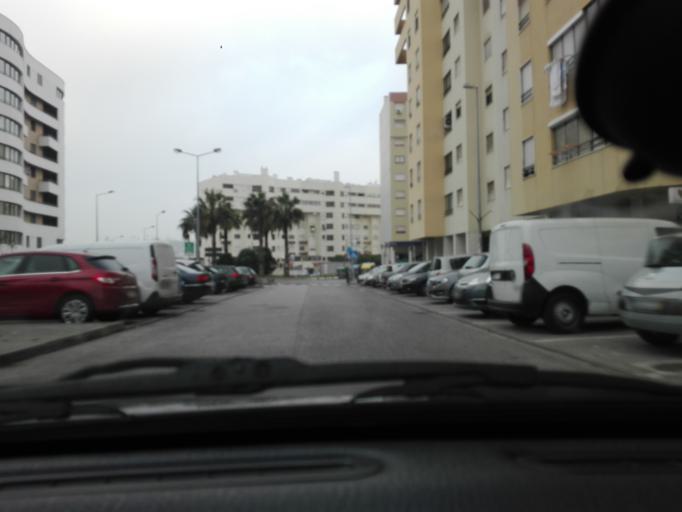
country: PT
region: Lisbon
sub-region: Loures
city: Loures
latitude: 38.8391
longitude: -9.1580
